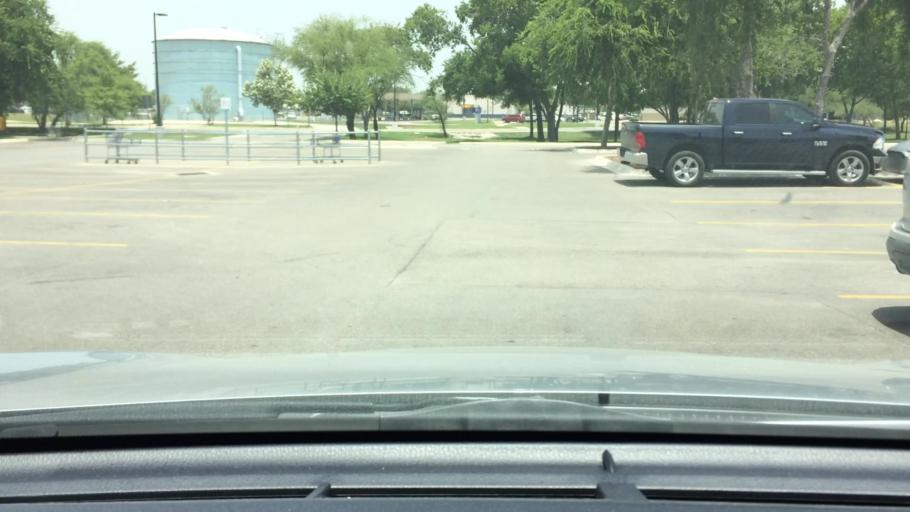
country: US
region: Texas
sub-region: Bexar County
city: China Grove
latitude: 29.3489
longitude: -98.4316
